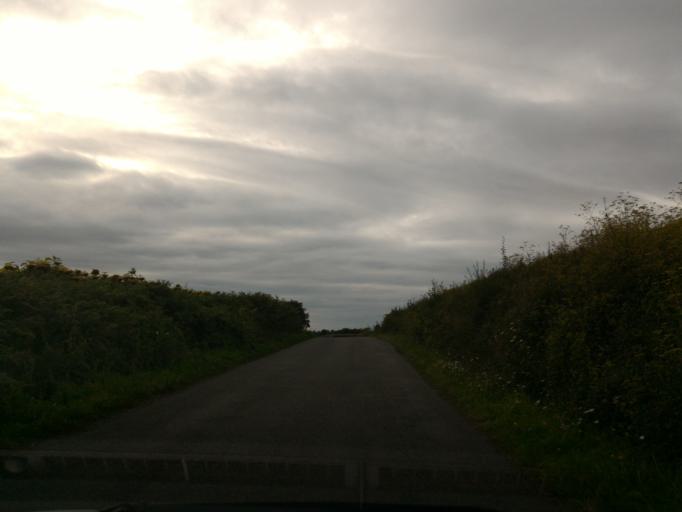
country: FR
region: Poitou-Charentes
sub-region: Departement de la Charente
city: Brigueuil
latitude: 45.9244
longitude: 0.8364
